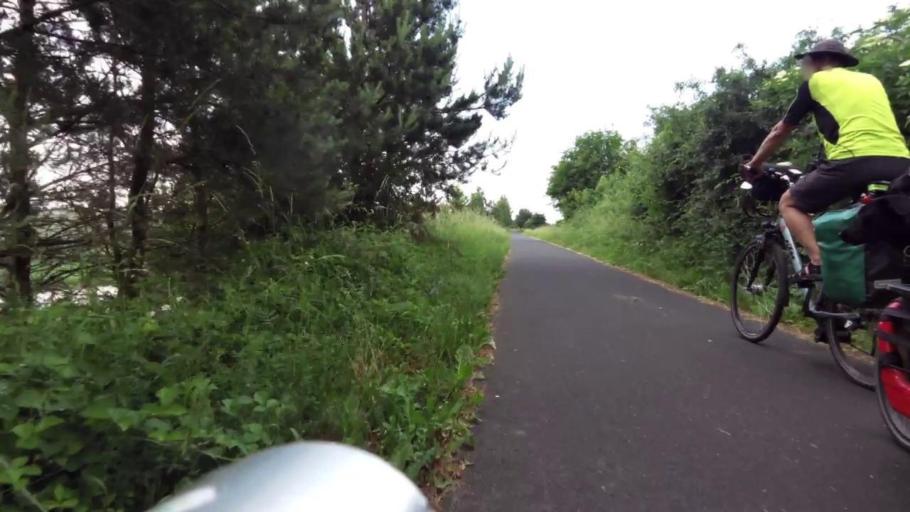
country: PL
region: Kujawsko-Pomorskie
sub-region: Powiat torunski
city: Lubianka
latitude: 53.1210
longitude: 18.4683
